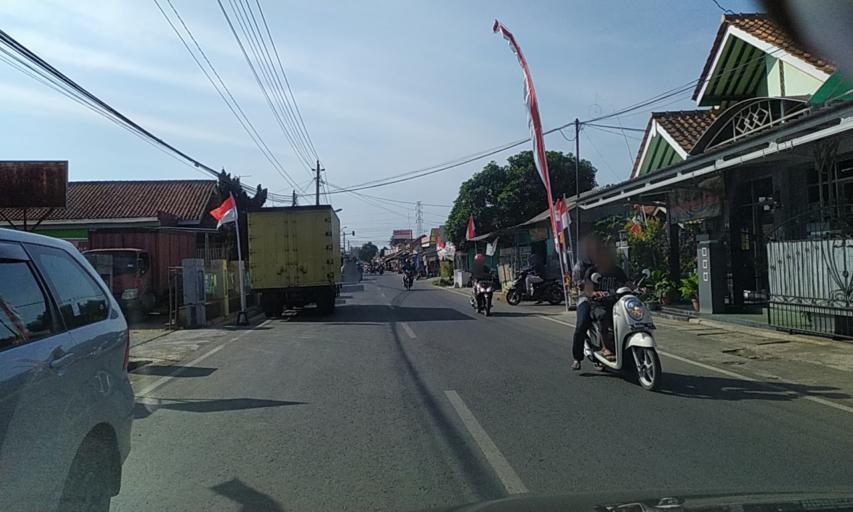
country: ID
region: Central Java
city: Rejanegara
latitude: -7.6736
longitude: 109.0521
